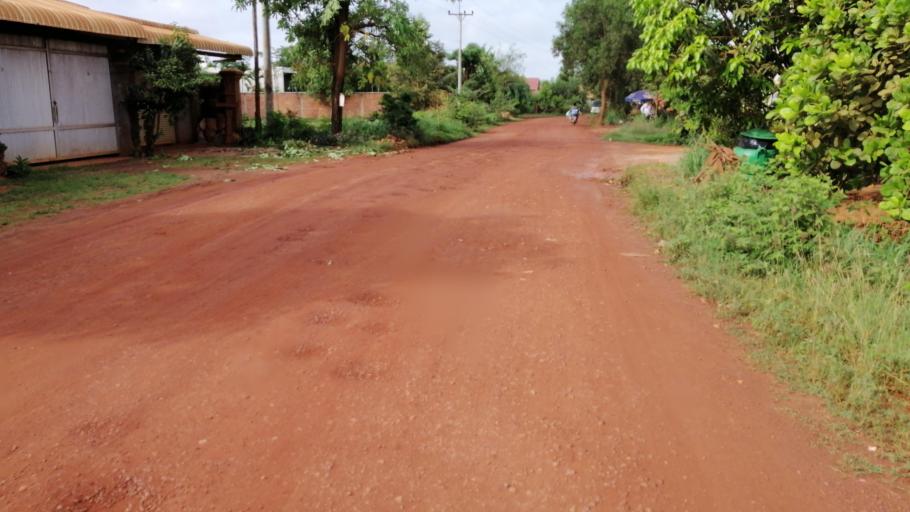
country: KH
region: Siem Reap
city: Siem Reap
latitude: 13.3616
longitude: 103.8300
